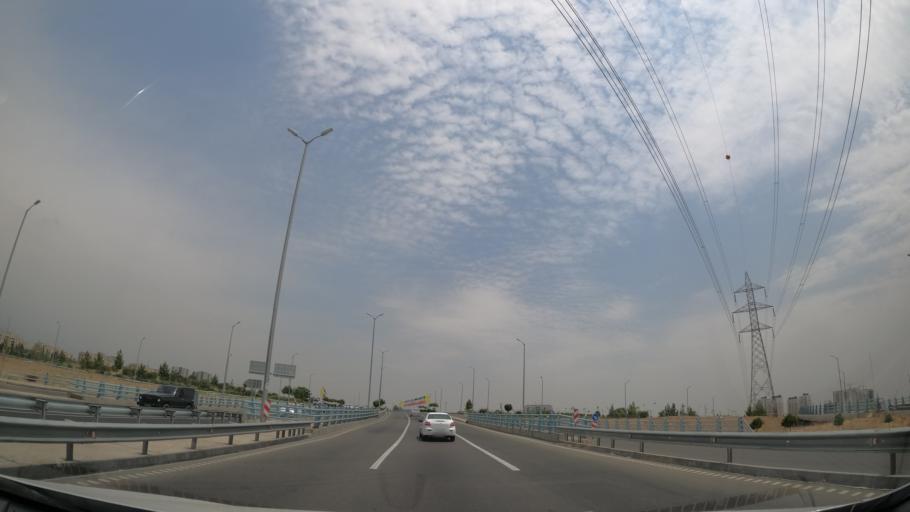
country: IR
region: Tehran
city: Shahr-e Qods
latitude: 35.7393
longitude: 51.2515
